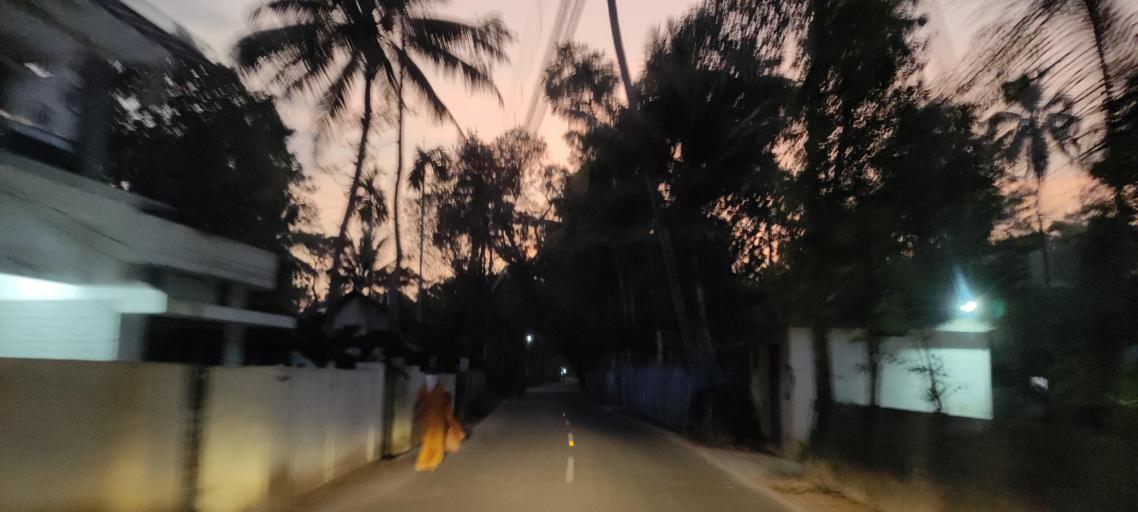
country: IN
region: Kerala
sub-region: Kottayam
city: Vaikam
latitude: 9.7745
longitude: 76.3667
